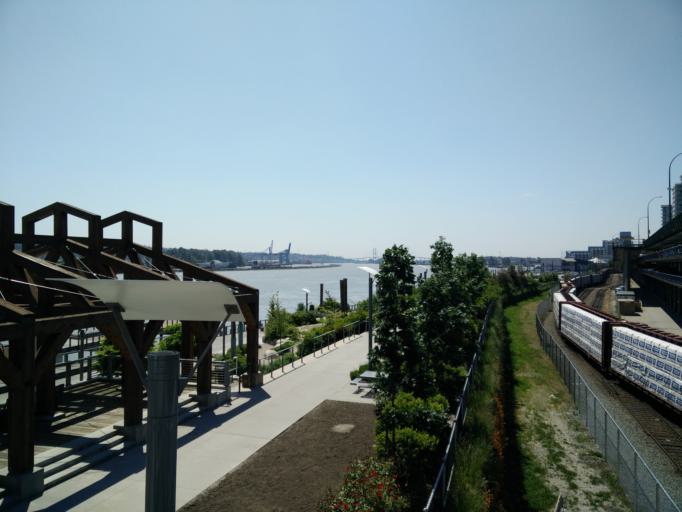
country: CA
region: British Columbia
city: New Westminster
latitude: 49.2040
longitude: -122.9047
